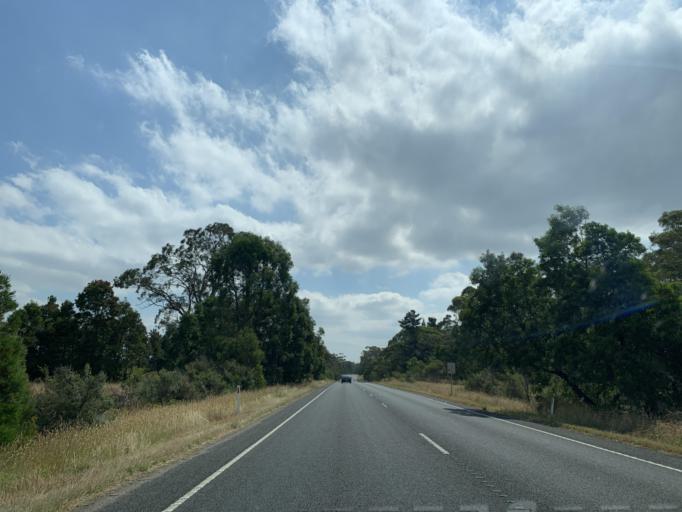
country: AU
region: Victoria
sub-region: Latrobe
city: Morwell
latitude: -38.2032
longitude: 146.4636
